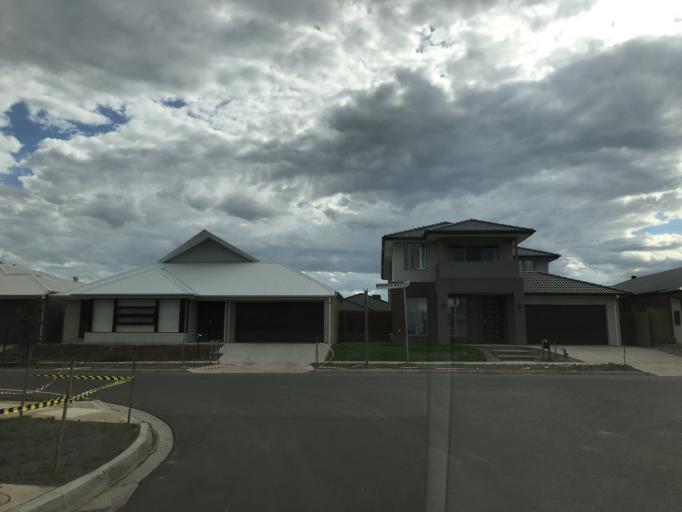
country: AU
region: Victoria
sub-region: Wyndham
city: Truganina
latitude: -37.8252
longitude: 144.7287
